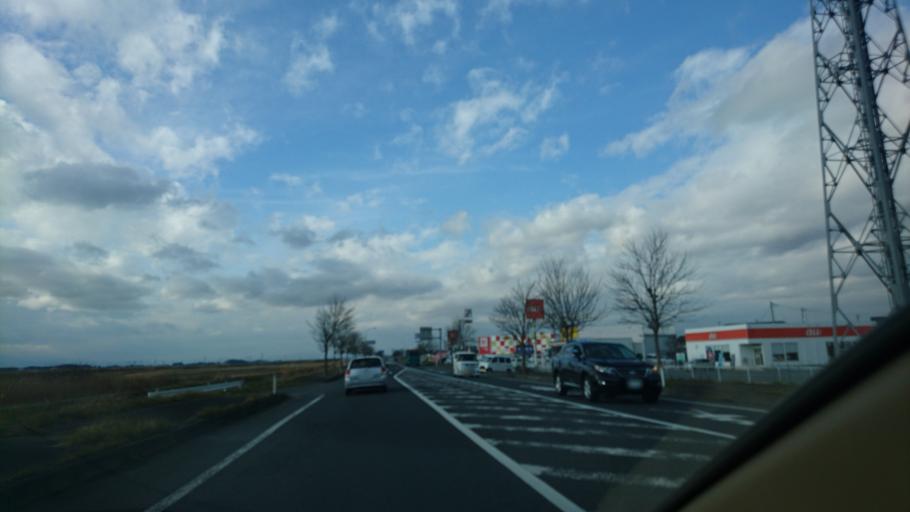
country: JP
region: Miyagi
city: Wakuya
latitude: 38.5309
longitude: 141.1300
